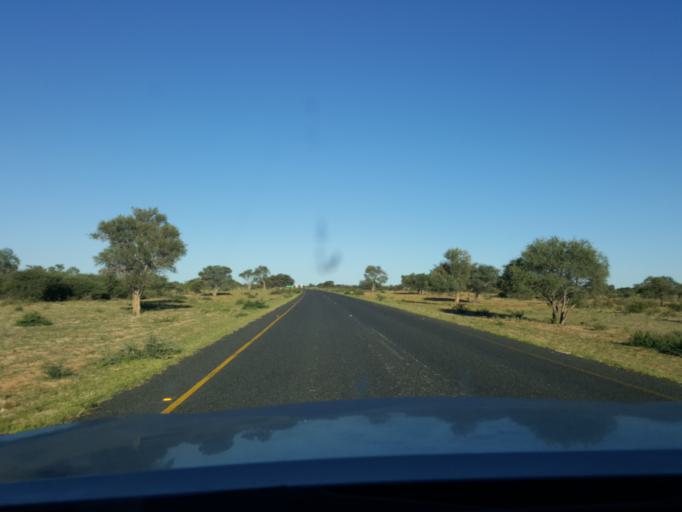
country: BW
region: Southern
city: Khakhea
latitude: -24.2552
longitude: 23.3016
